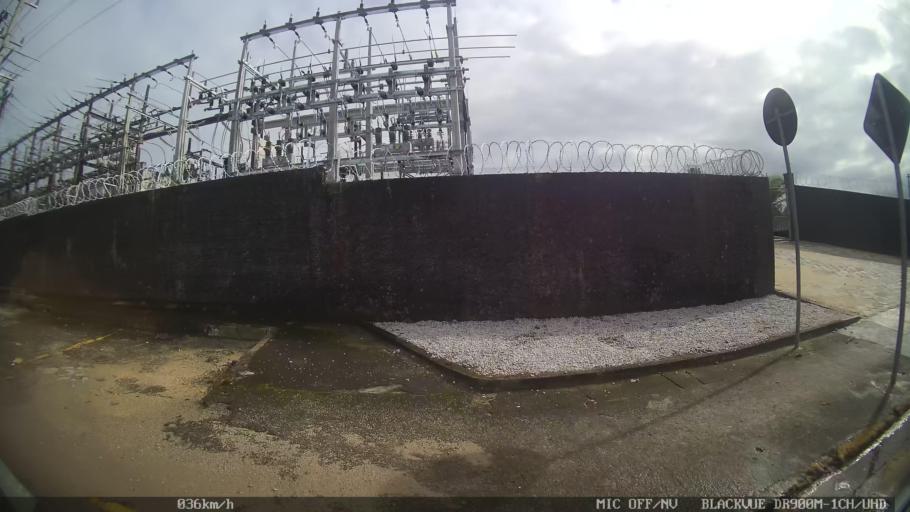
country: BR
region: Santa Catarina
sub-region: Biguacu
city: Biguacu
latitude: -27.5067
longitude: -48.6571
